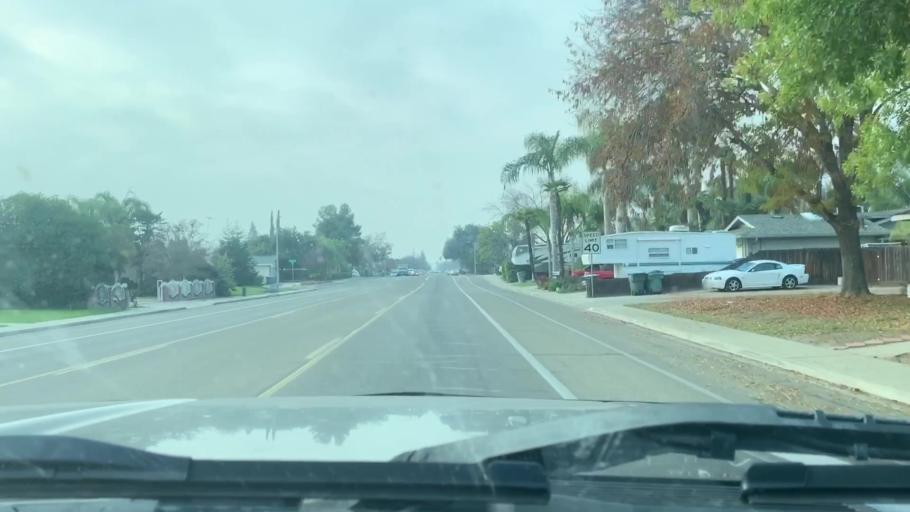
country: US
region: California
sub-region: Tulare County
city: Visalia
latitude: 36.3057
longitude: -119.3073
